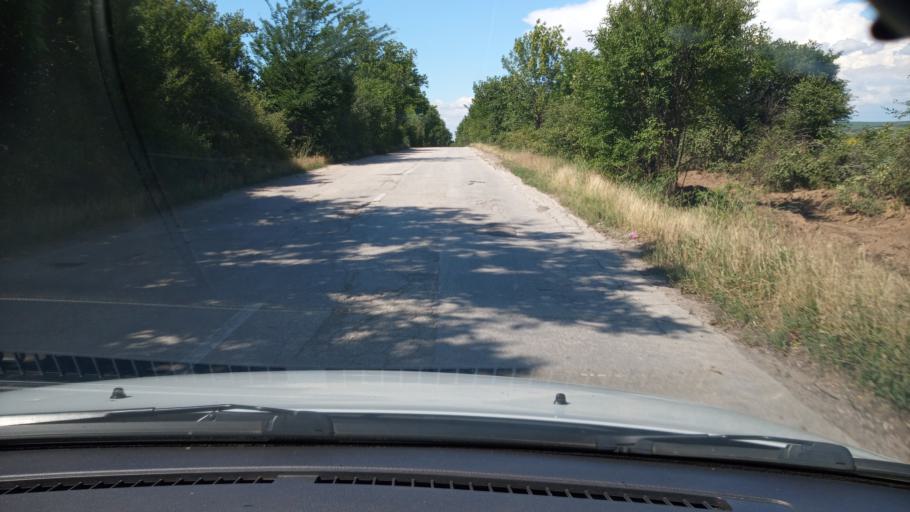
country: BG
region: Pleven
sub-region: Obshtina Dolna Mitropoliya
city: Dolna Mitropoliya
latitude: 43.4427
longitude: 24.5274
